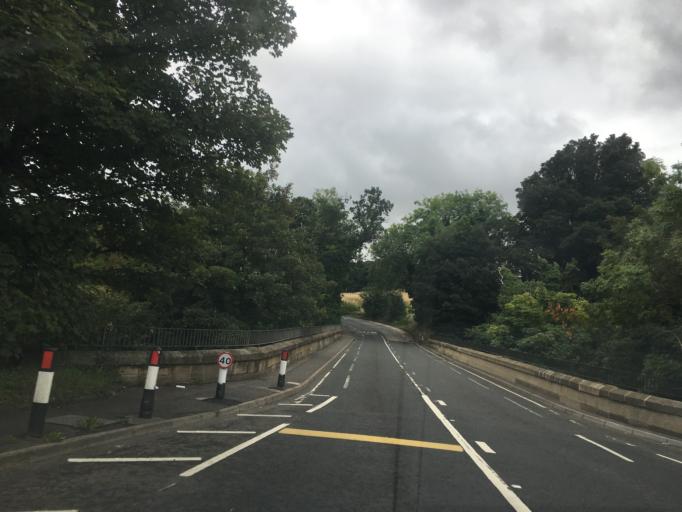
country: GB
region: Scotland
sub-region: Midlothian
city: Dalkeith
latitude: 55.8927
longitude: -3.0870
